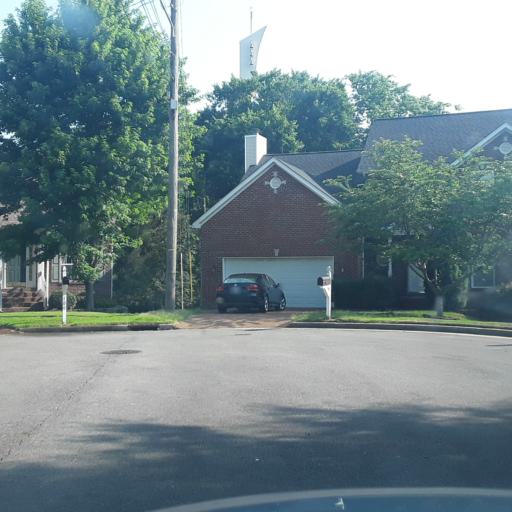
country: US
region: Tennessee
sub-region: Williamson County
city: Brentwood Estates
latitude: 36.0352
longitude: -86.7158
